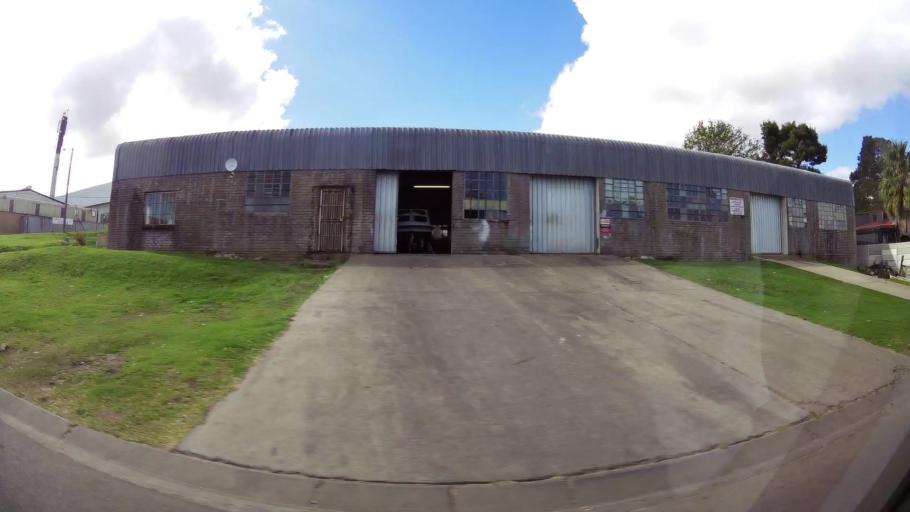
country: ZA
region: Western Cape
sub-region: Eden District Municipality
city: Knysna
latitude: -34.0449
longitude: 23.0837
